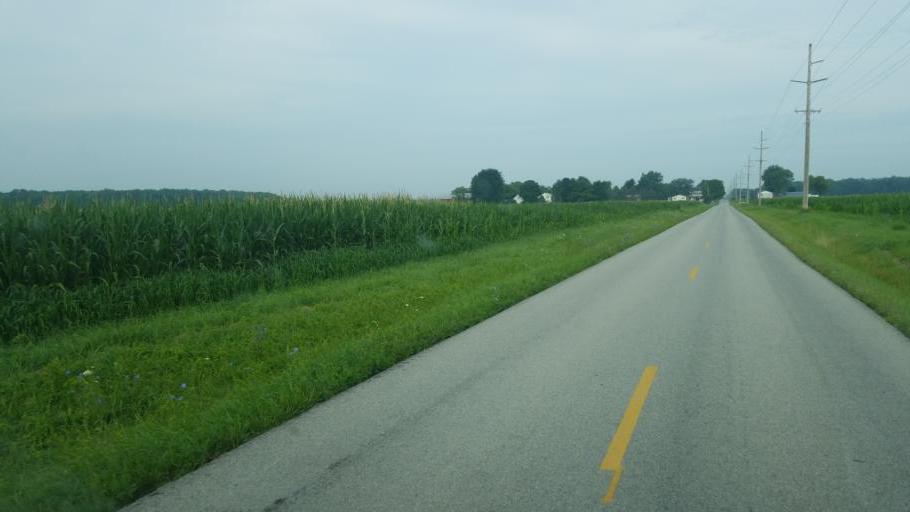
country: US
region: Ohio
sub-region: Morrow County
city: Cardington
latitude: 40.4683
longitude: -82.9226
